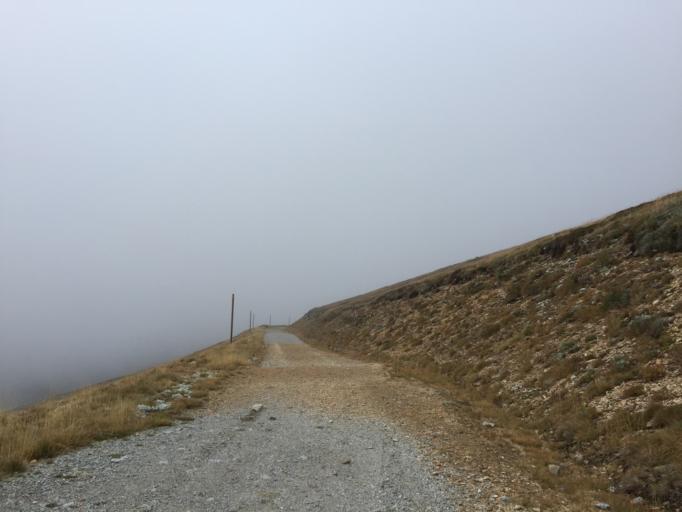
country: AU
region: New South Wales
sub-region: Snowy River
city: Jindabyne
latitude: -36.4549
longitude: 148.2731
